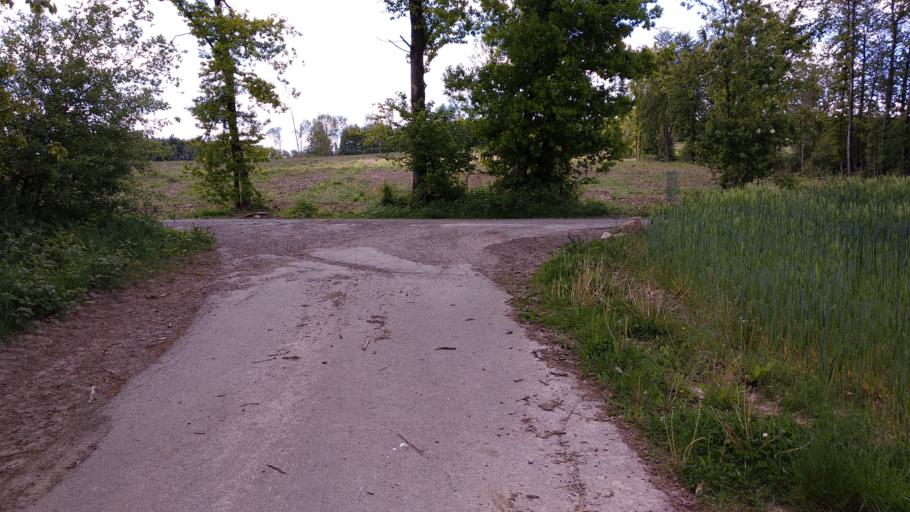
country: DE
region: North Rhine-Westphalia
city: Beverungen
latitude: 51.6728
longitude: 9.3235
